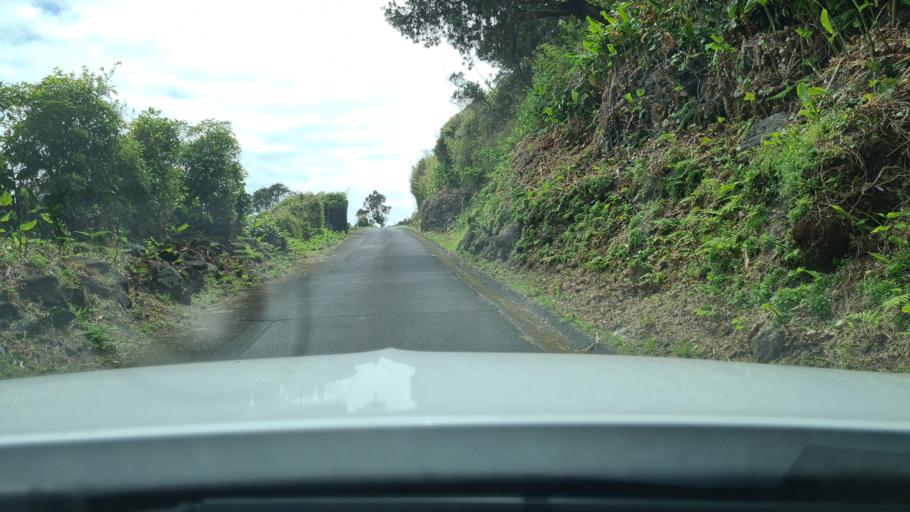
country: PT
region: Azores
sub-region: Sao Roque do Pico
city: Sao Roque do Pico
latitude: 38.6389
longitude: -27.9671
